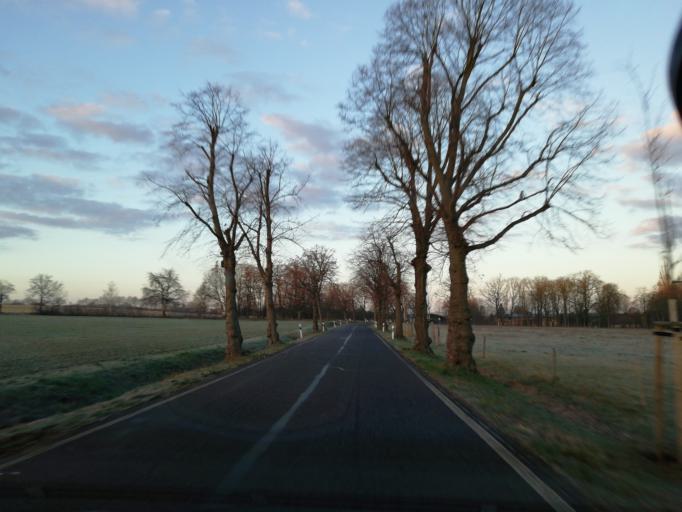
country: DE
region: Brandenburg
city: Calau
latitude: 51.7352
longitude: 13.9175
